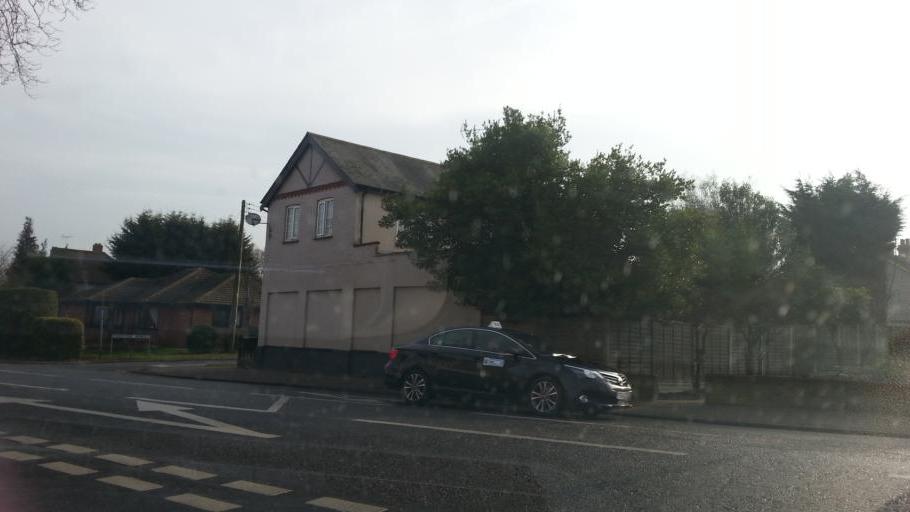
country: GB
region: England
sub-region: Essex
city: Hadleigh
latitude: 51.5604
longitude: 0.5925
